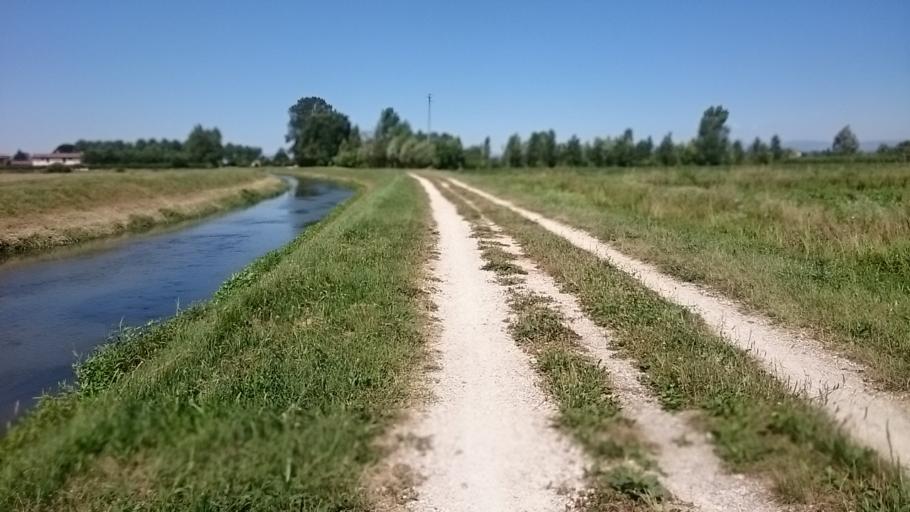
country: IT
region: Veneto
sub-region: Provincia di Padova
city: Pionca
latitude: 45.4685
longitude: 11.9566
